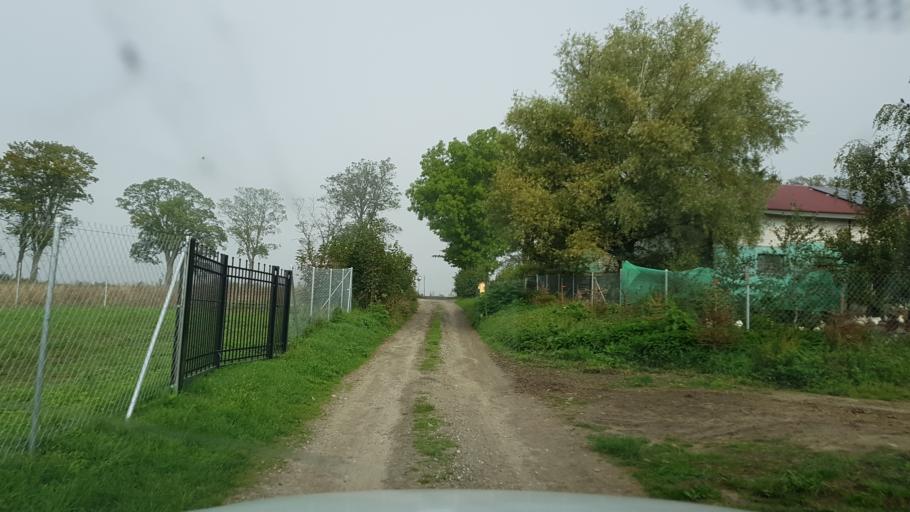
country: PL
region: West Pomeranian Voivodeship
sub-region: Powiat koszalinski
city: Mielno
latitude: 54.2365
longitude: 15.9596
